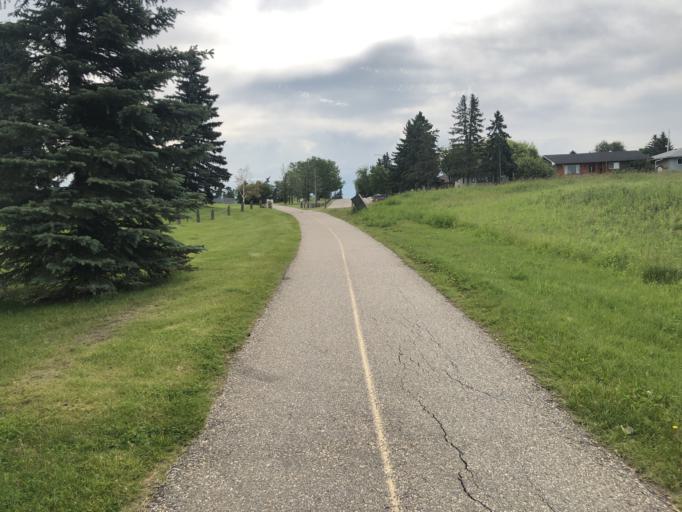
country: CA
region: Alberta
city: Calgary
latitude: 51.0743
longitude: -114.0225
